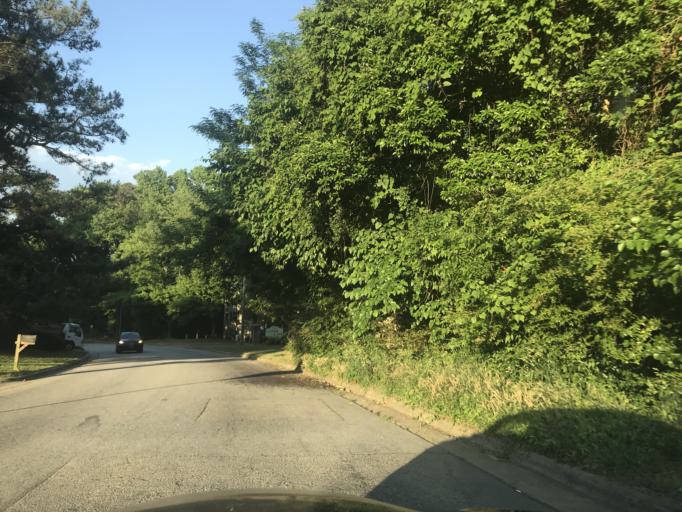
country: US
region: North Carolina
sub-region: Wake County
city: Raleigh
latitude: 35.7450
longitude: -78.6581
